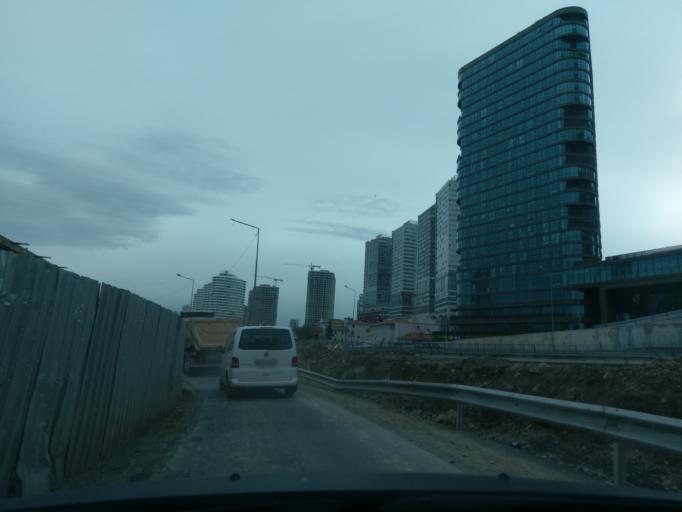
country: TR
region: Istanbul
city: UEskuedar
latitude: 40.9972
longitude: 29.0562
